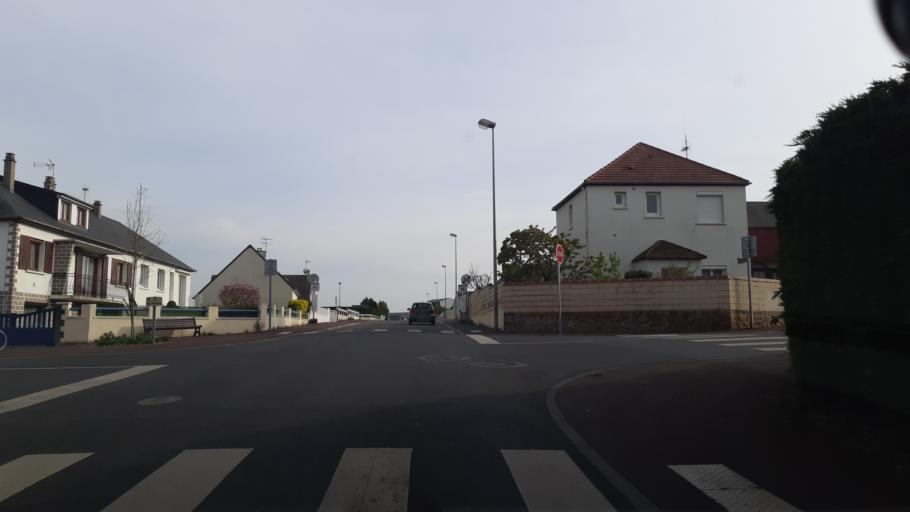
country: FR
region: Lower Normandy
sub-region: Departement de la Manche
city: Donville-les-Bains
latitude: 48.8410
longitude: -1.5785
